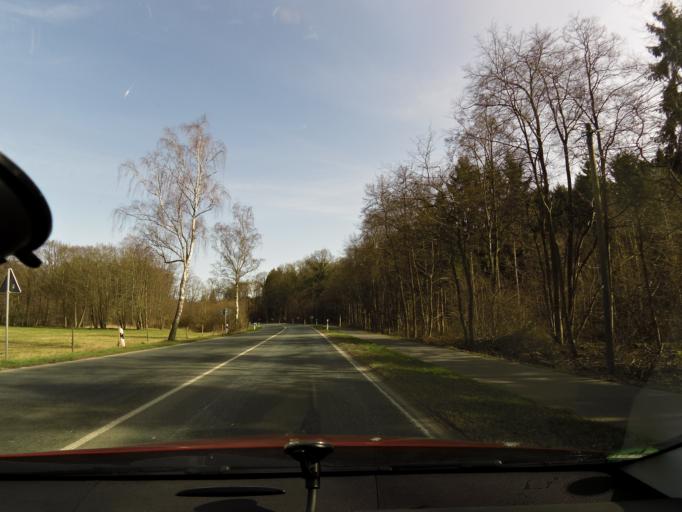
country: DE
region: North Rhine-Westphalia
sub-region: Regierungsbezirk Koln
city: Alfter
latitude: 50.6891
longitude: 6.9949
